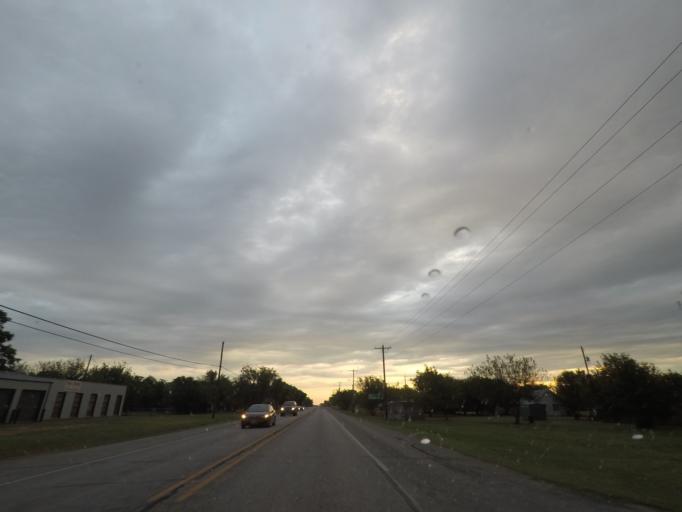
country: US
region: Texas
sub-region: Clay County
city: Henrietta
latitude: 34.0140
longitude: -98.2318
